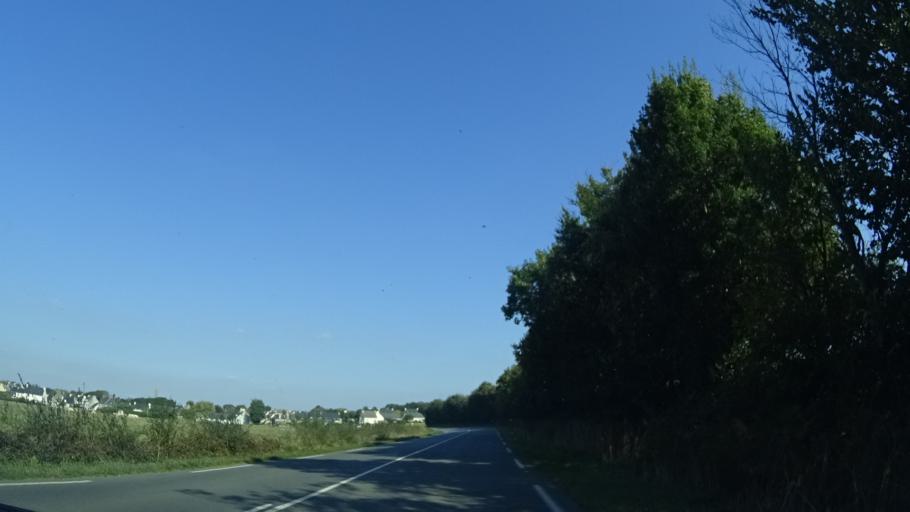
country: FR
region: Brittany
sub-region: Departement du Finistere
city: Plonevez-Porzay
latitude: 48.1209
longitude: -4.2279
